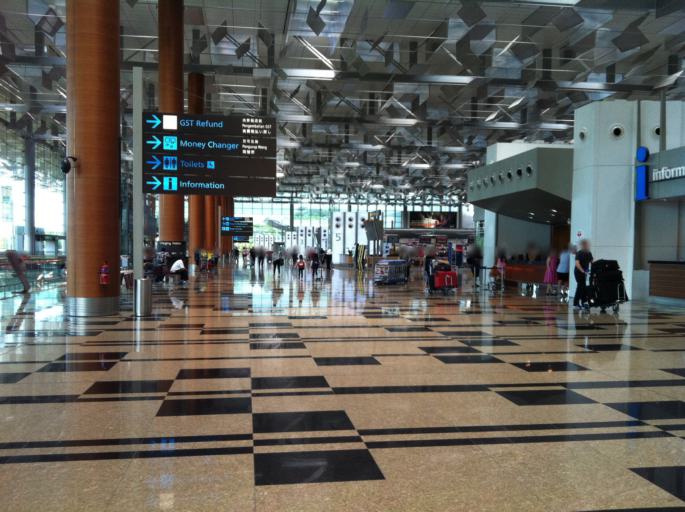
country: SG
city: Singapore
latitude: 1.3566
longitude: 103.9873
